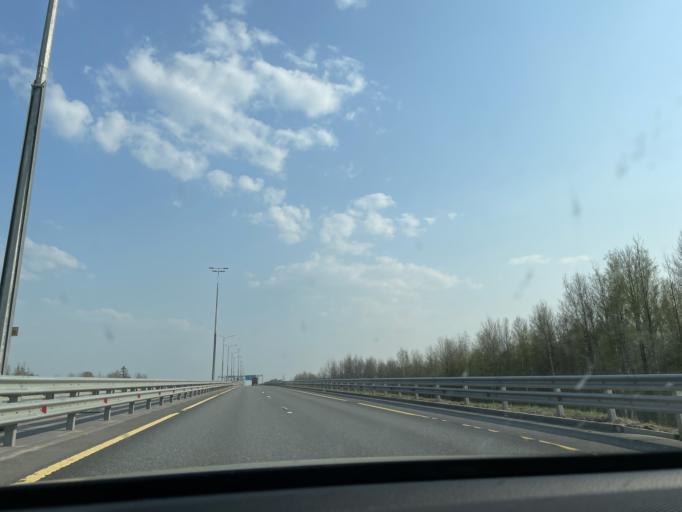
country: RU
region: Novgorod
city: Krechevitsy
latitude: 58.8074
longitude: 31.4560
